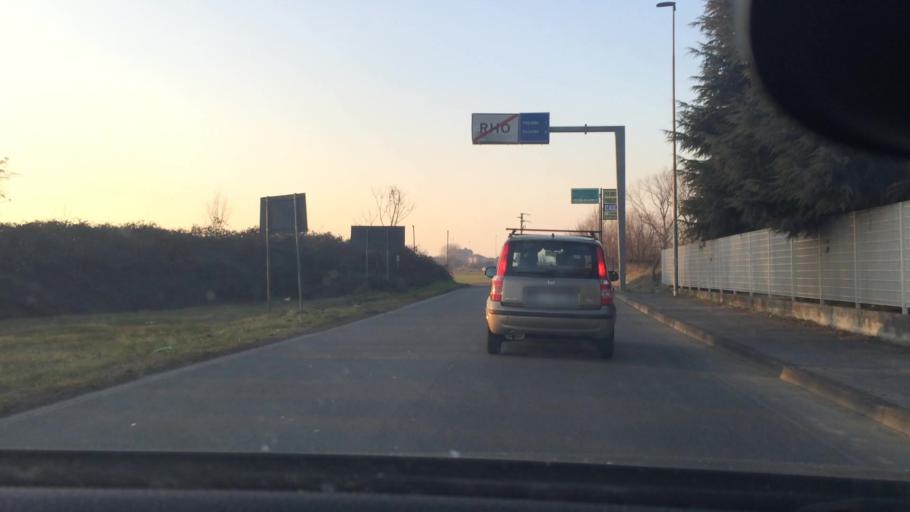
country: IT
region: Lombardy
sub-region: Citta metropolitana di Milano
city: Pogliano Milanese
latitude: 45.5360
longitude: 9.0114
